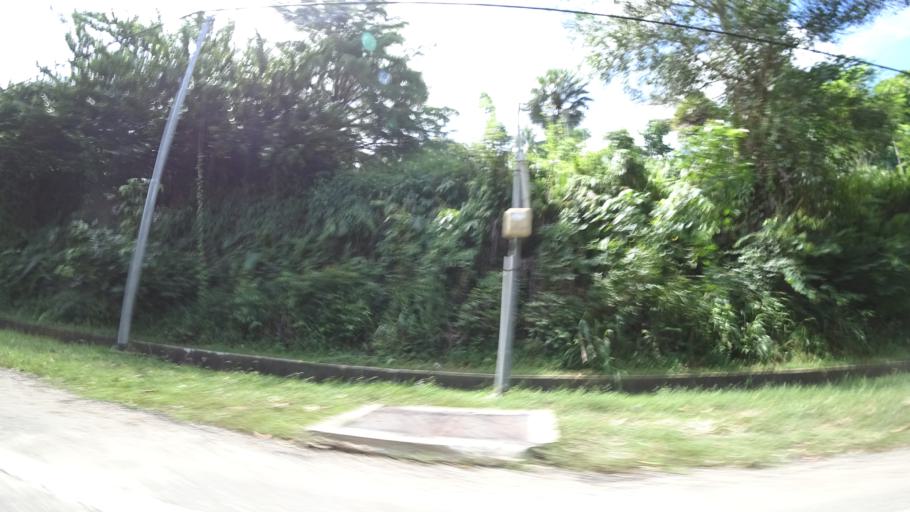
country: BN
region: Brunei and Muara
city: Bandar Seri Begawan
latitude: 4.8868
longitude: 114.9708
